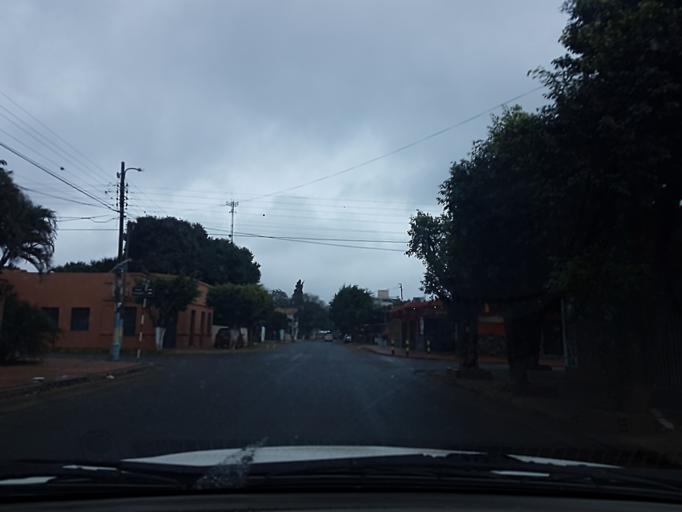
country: PY
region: Central
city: San Lorenzo
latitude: -25.2686
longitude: -57.4826
